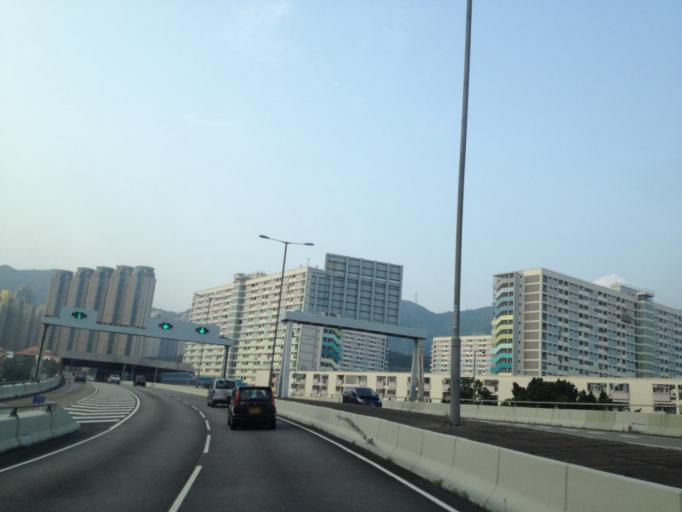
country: HK
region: Wong Tai Sin
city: Wong Tai Sin
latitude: 22.3338
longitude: 114.2051
